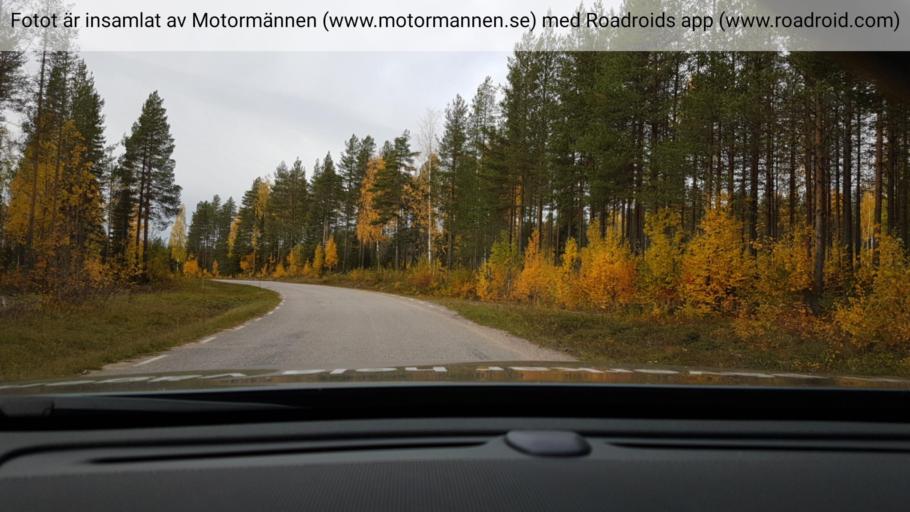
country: SE
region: Norrbotten
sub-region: Overkalix Kommun
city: OEverkalix
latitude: 66.2601
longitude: 23.1076
